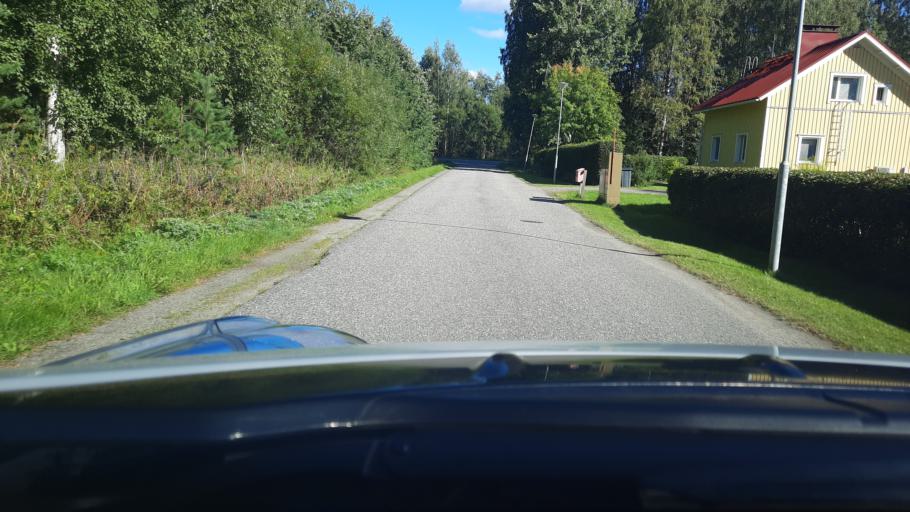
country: FI
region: North Karelia
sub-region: Joensuu
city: Joensuu
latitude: 62.6369
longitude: 29.6893
